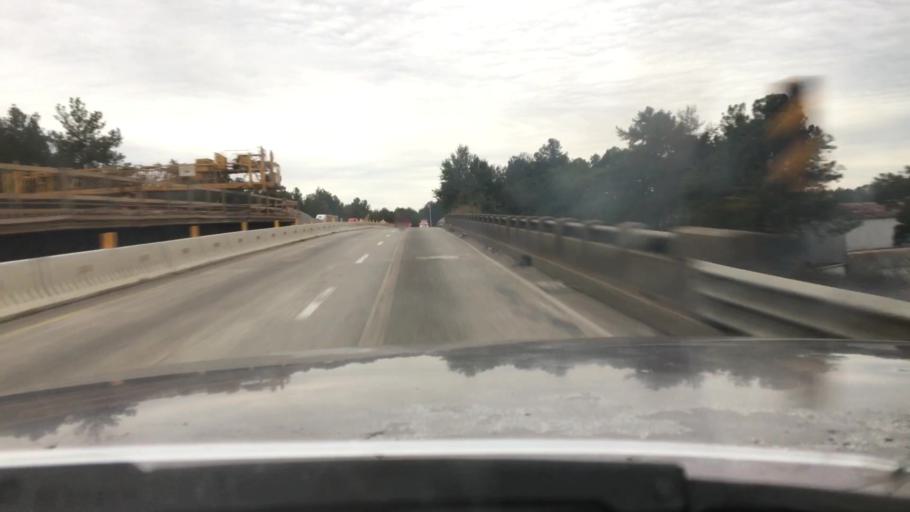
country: US
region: South Carolina
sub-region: Lexington County
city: Lexington
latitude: 33.9736
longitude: -81.1971
